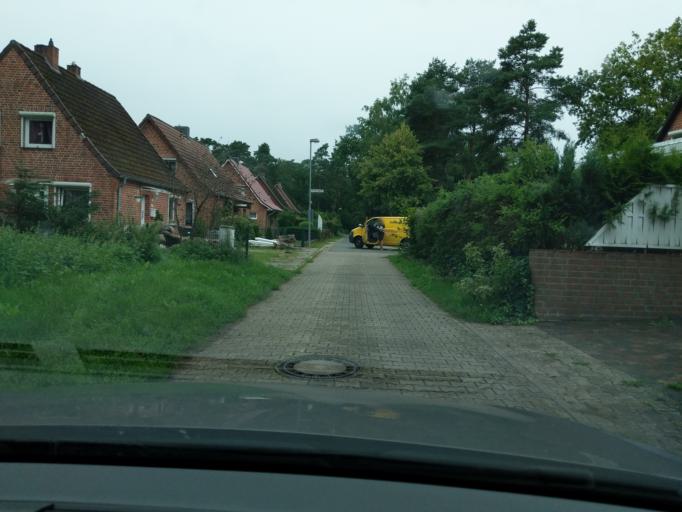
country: DE
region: Schleswig-Holstein
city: Schnakenbek
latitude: 53.3830
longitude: 10.5010
